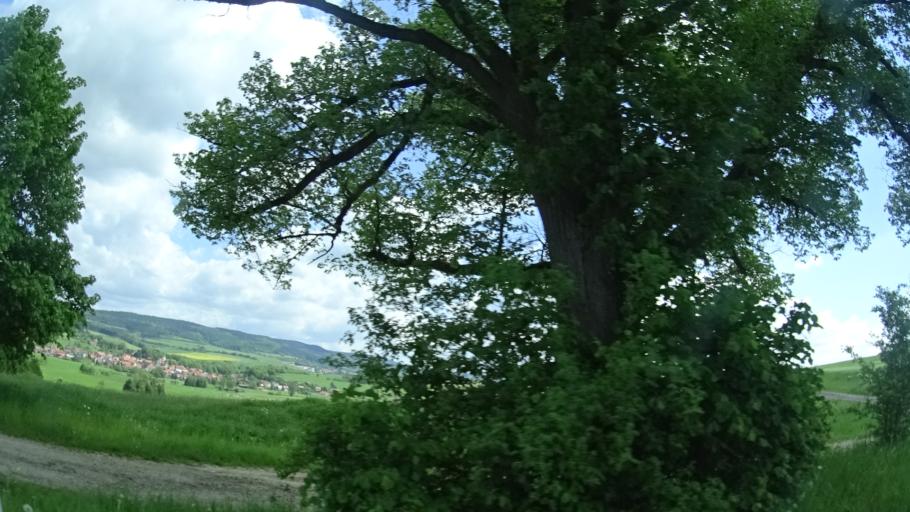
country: DE
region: Thuringia
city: Marisfeld
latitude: 50.5495
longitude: 10.5567
